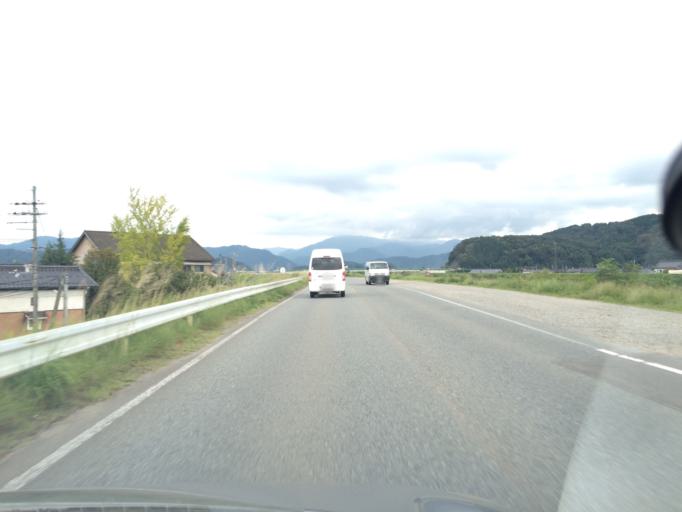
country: JP
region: Hyogo
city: Toyooka
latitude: 35.5128
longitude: 134.8273
